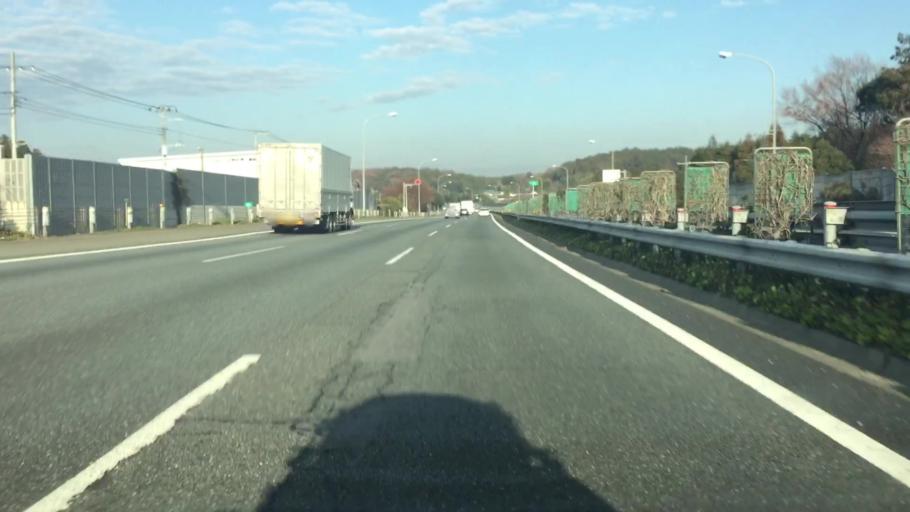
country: JP
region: Saitama
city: Ogawa
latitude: 36.0493
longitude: 139.3441
